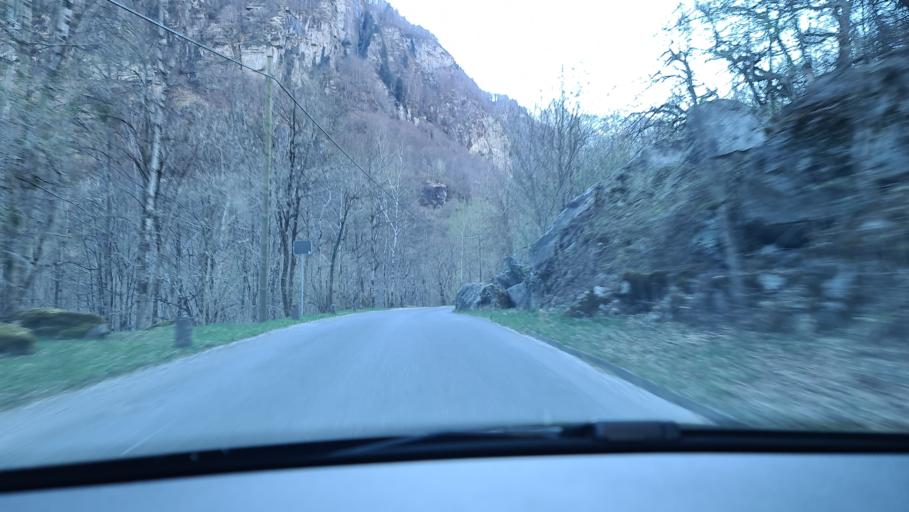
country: CH
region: Ticino
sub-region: Vallemaggia District
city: Cevio
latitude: 46.3624
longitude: 8.5757
